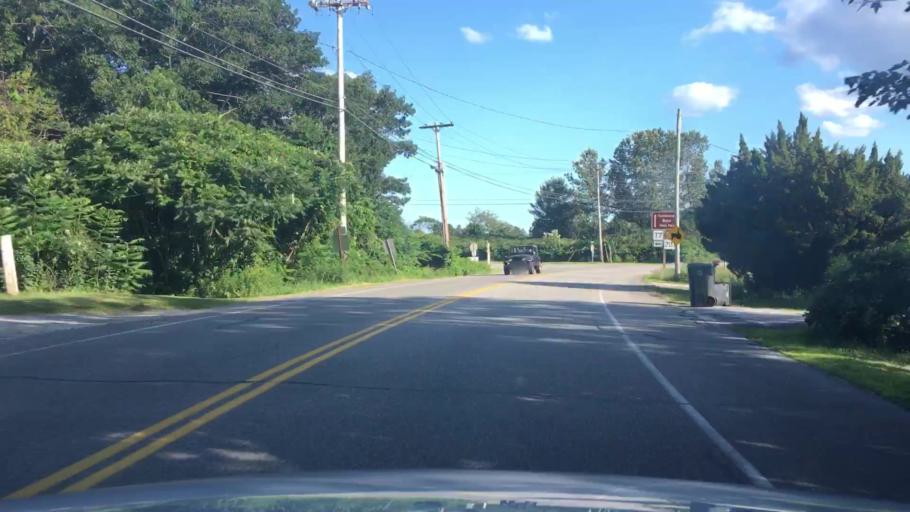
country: US
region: Maine
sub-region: Cumberland County
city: Scarborough
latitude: 43.5588
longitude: -70.3041
